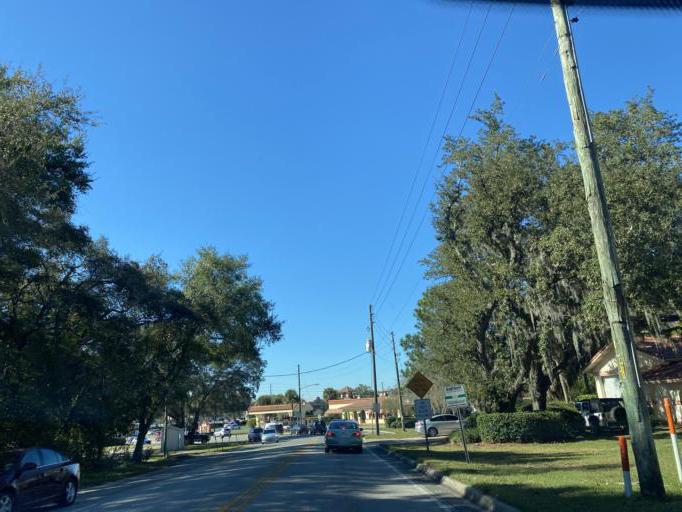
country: US
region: Florida
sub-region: Sumter County
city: The Villages
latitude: 28.9380
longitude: -81.9401
